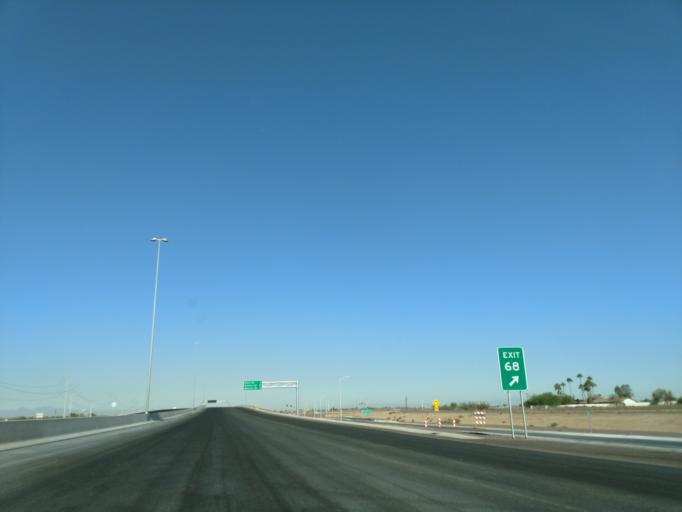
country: US
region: Arizona
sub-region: Maricopa County
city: Laveen
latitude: 33.3307
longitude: -112.1731
